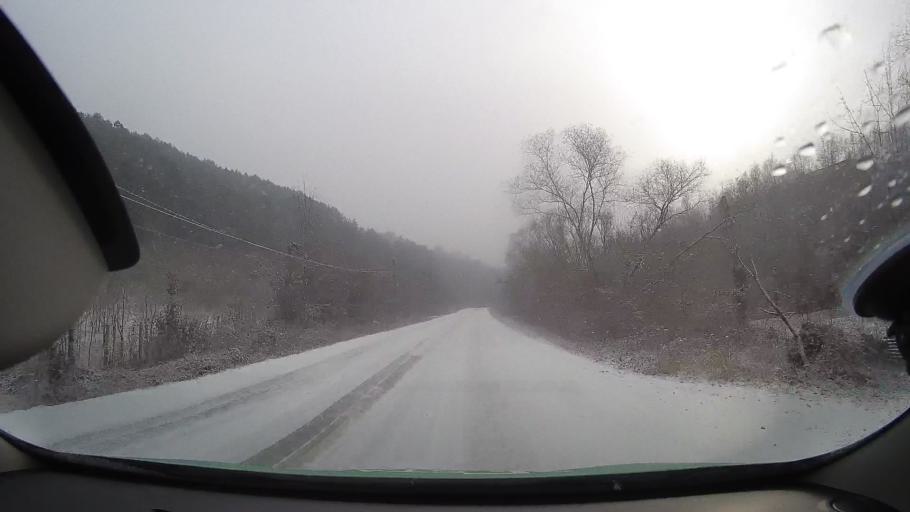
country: RO
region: Alba
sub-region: Comuna Livezile
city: Livezile
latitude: 46.3553
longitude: 23.6167
